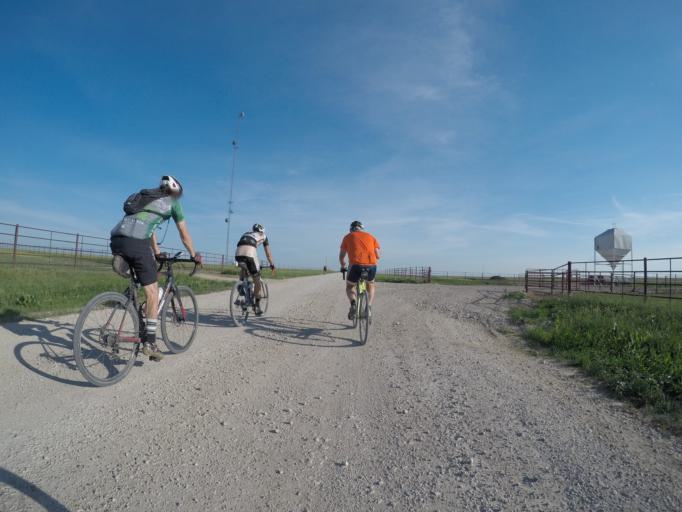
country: US
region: Kansas
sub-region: Riley County
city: Manhattan
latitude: 39.0303
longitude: -96.4917
